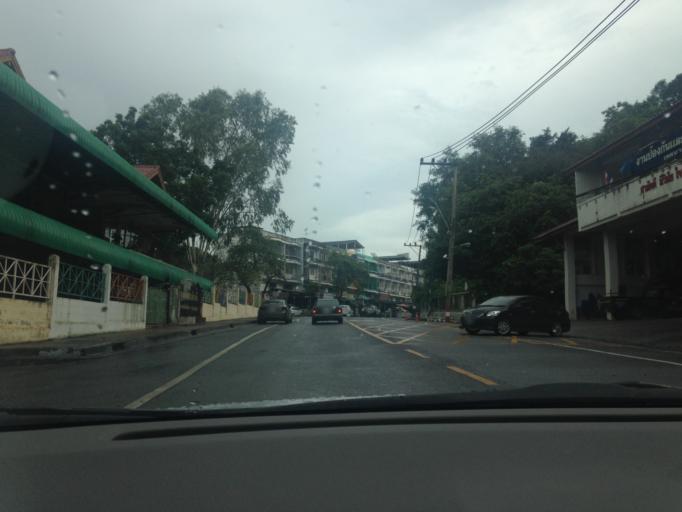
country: TH
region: Chon Buri
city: Si Racha
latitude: 13.1614
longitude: 100.9226
